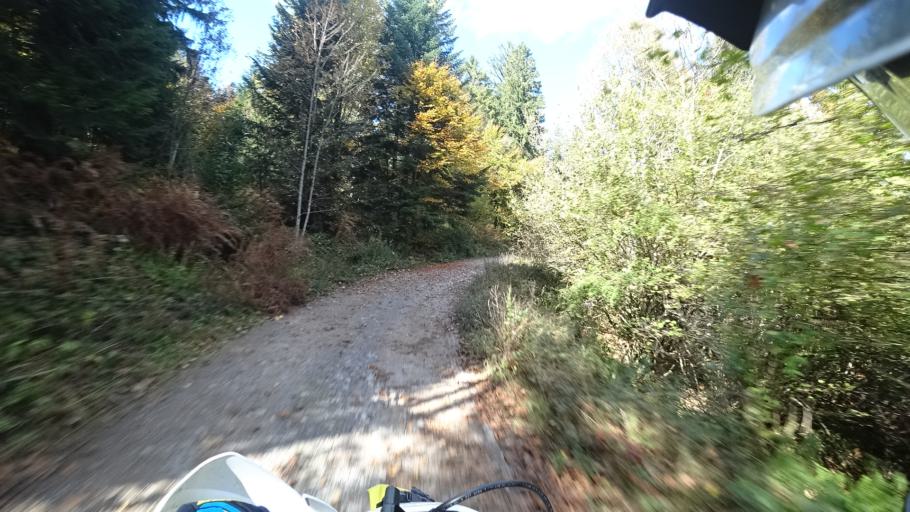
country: HR
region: Karlovacka
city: Plaski
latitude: 45.0687
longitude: 15.3463
